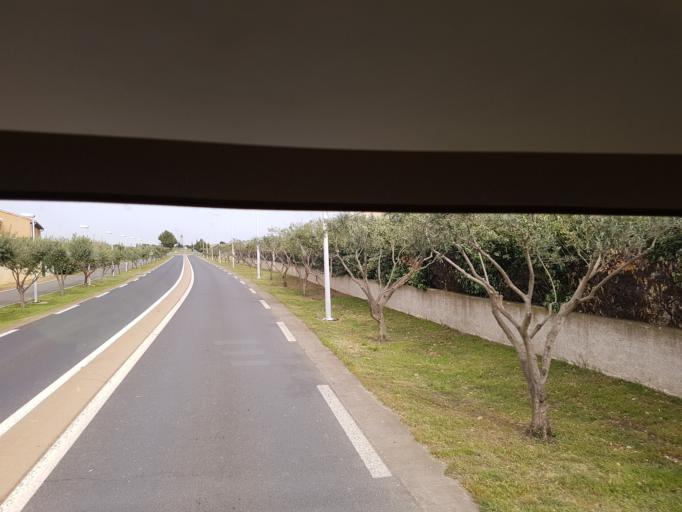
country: FR
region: Languedoc-Roussillon
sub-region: Departement de l'Herault
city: Vendres
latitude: 43.2694
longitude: 3.2298
